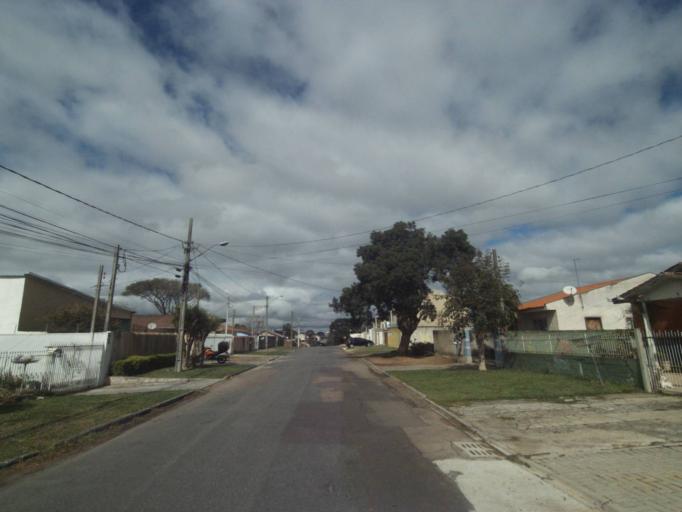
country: BR
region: Parana
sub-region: Sao Jose Dos Pinhais
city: Sao Jose dos Pinhais
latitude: -25.5380
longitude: -49.2908
